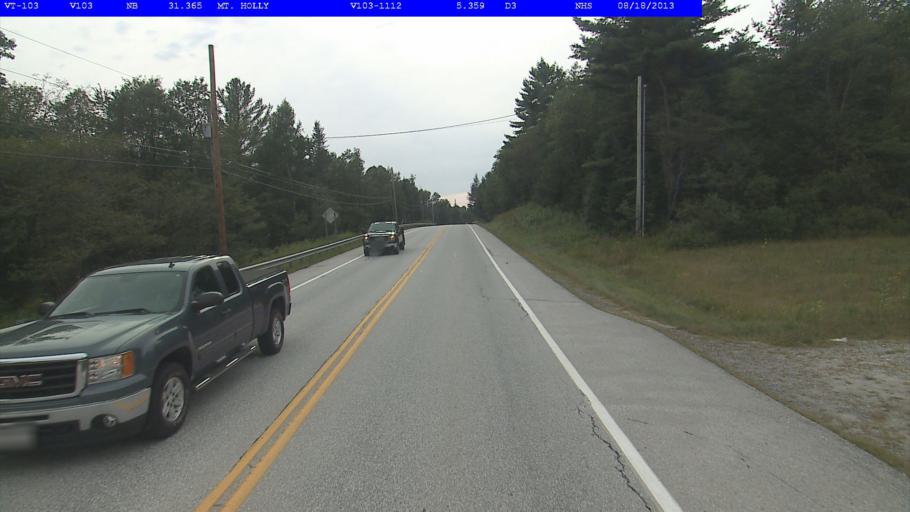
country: US
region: Vermont
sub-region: Rutland County
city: Rutland
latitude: 43.4475
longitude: -72.8276
